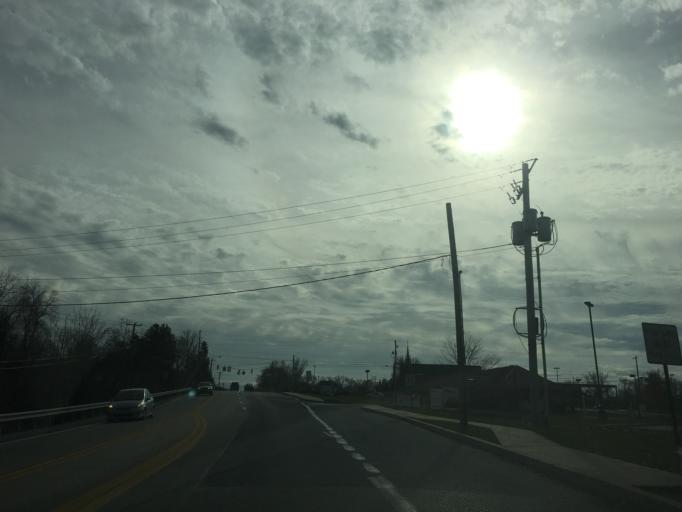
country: US
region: Pennsylvania
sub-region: Dauphin County
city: Colonial Park
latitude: 40.3080
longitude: -76.8238
